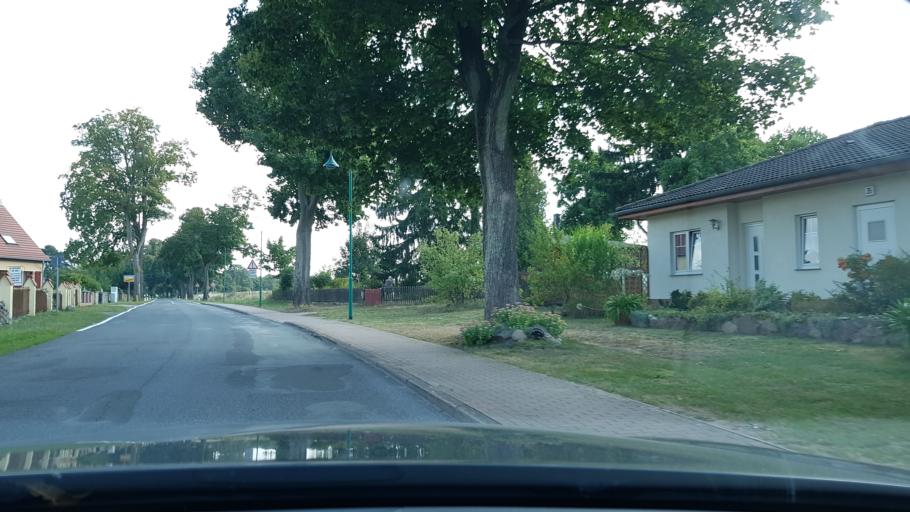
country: DE
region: Brandenburg
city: Lindow
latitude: 52.9893
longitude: 12.9727
